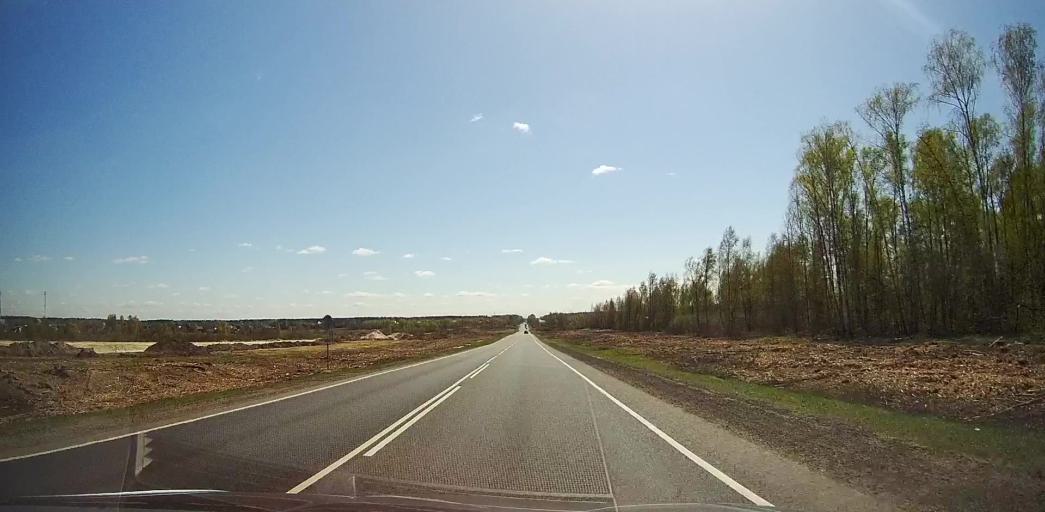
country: RU
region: Moskovskaya
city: Gzhel'
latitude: 55.5838
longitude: 38.3860
